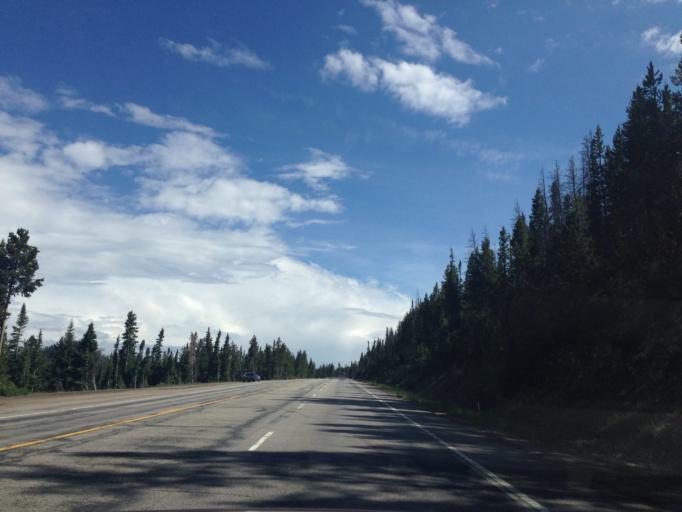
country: US
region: Colorado
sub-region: Routt County
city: Steamboat Springs
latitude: 40.3916
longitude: -106.6101
